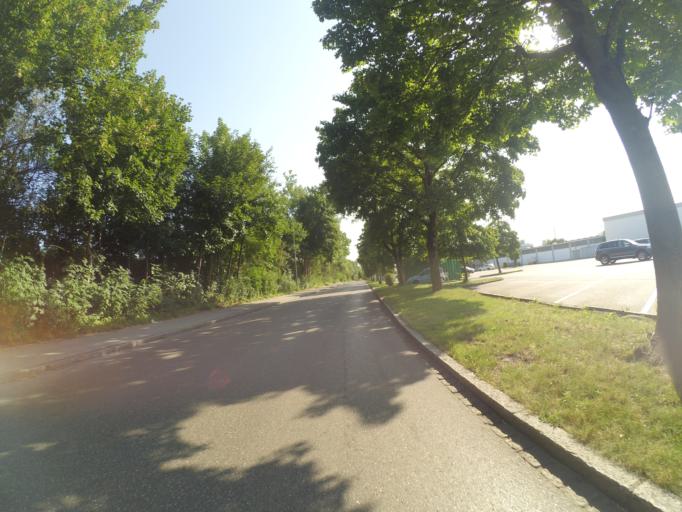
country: DE
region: Bavaria
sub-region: Swabia
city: Buchloe
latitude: 48.0394
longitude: 10.7197
